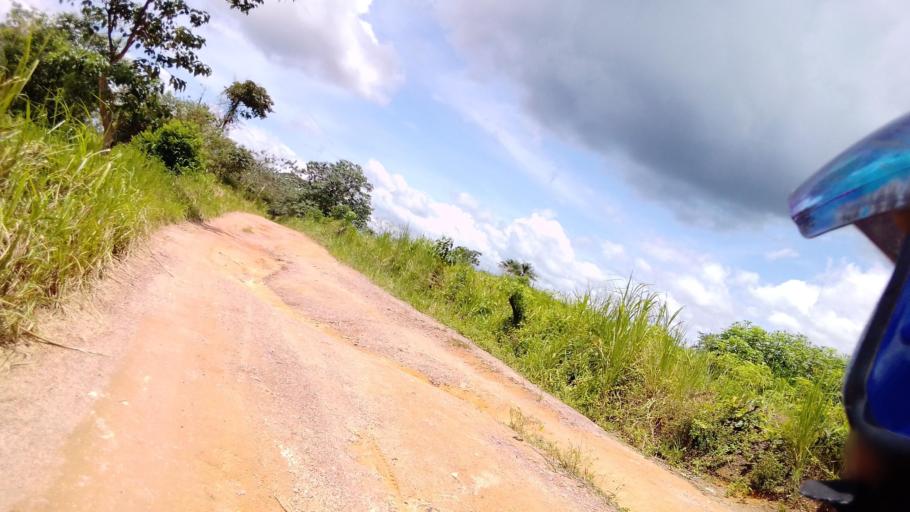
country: SL
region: Eastern Province
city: Koidu
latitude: 8.6921
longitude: -10.9542
